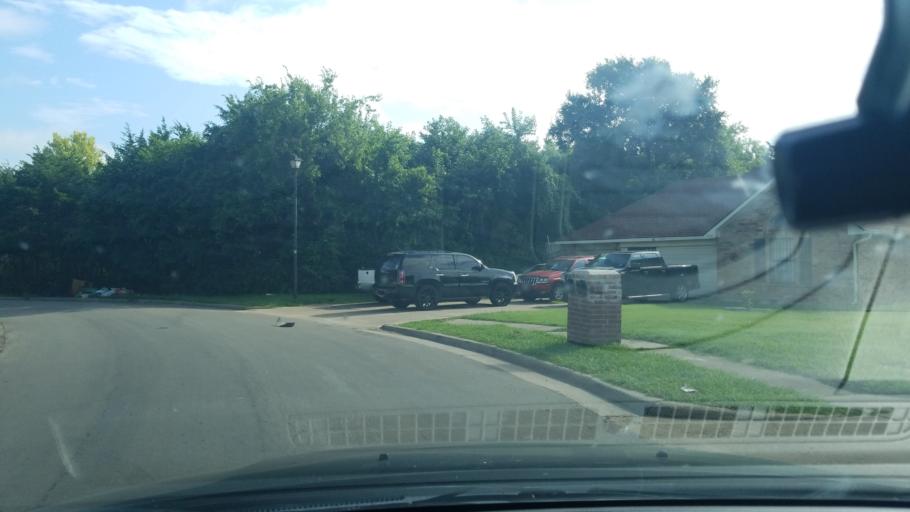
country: US
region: Texas
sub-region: Dallas County
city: Balch Springs
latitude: 32.7412
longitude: -96.6632
